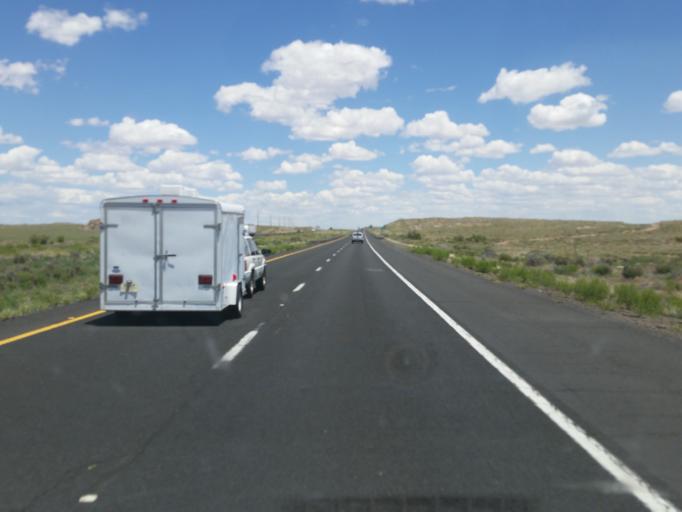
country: US
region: Arizona
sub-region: Navajo County
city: Holbrook
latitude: 34.9911
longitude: -109.9861
